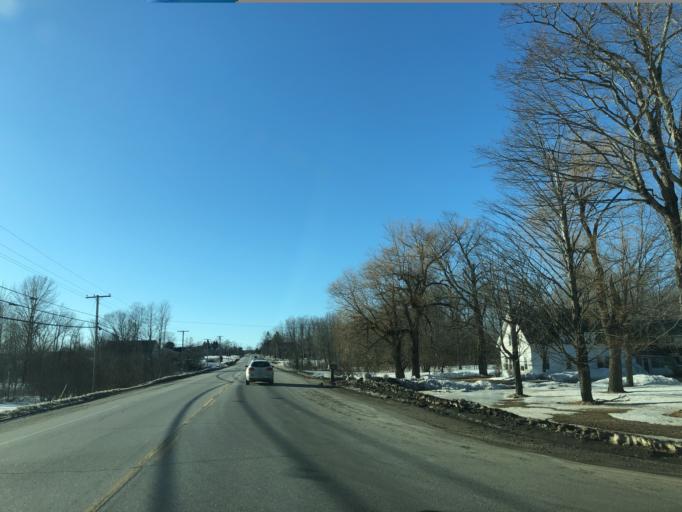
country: US
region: Maine
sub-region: Penobscot County
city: Kenduskeag
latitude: 44.9859
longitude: -69.0075
